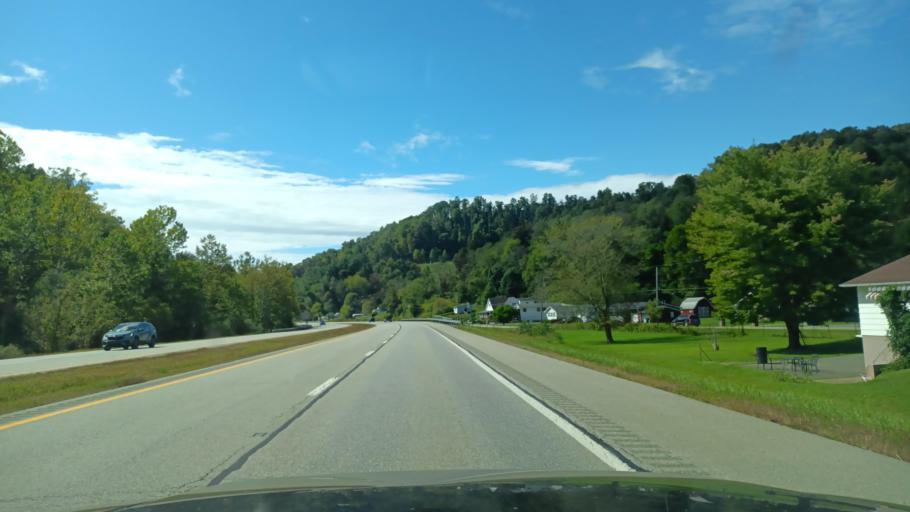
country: US
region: West Virginia
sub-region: Harrison County
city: Salem
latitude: 39.2938
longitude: -80.6303
